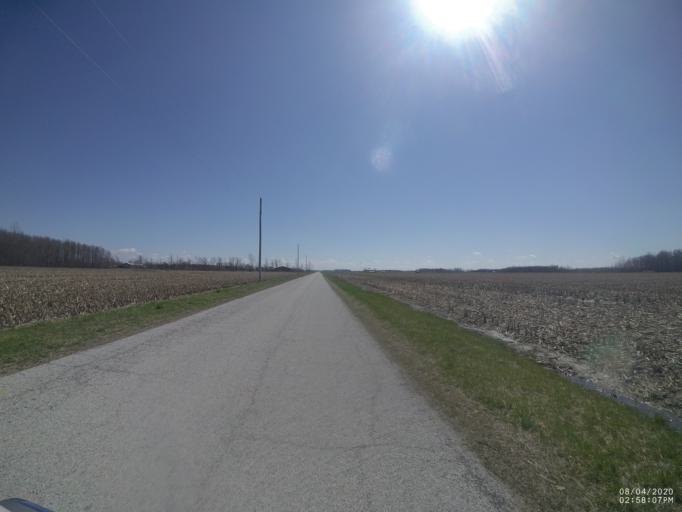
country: US
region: Ohio
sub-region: Sandusky County
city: Gibsonburg
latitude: 41.3287
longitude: -83.2542
